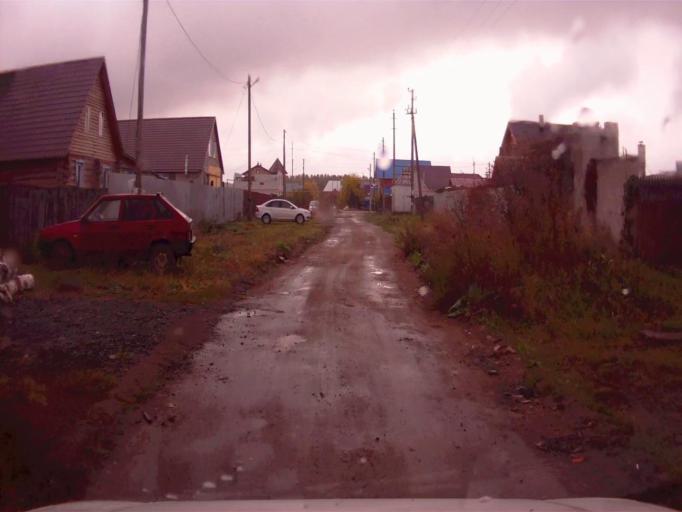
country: RU
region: Chelyabinsk
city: Dolgoderevenskoye
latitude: 55.3061
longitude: 61.3415
